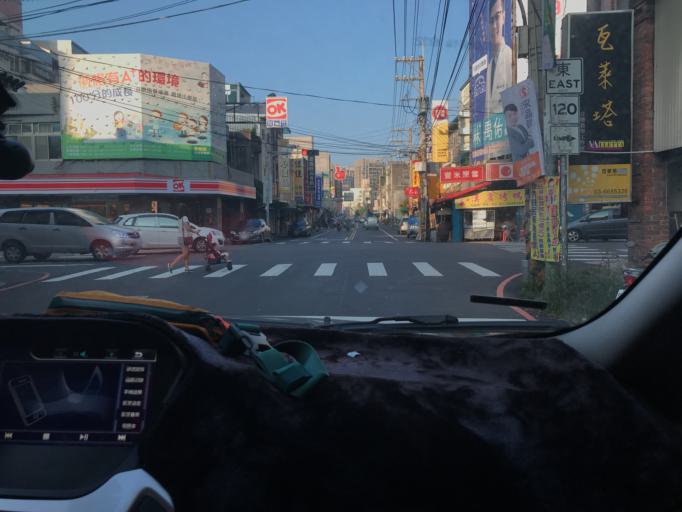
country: TW
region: Taiwan
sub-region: Hsinchu
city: Zhubei
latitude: 24.8194
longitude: 121.0302
